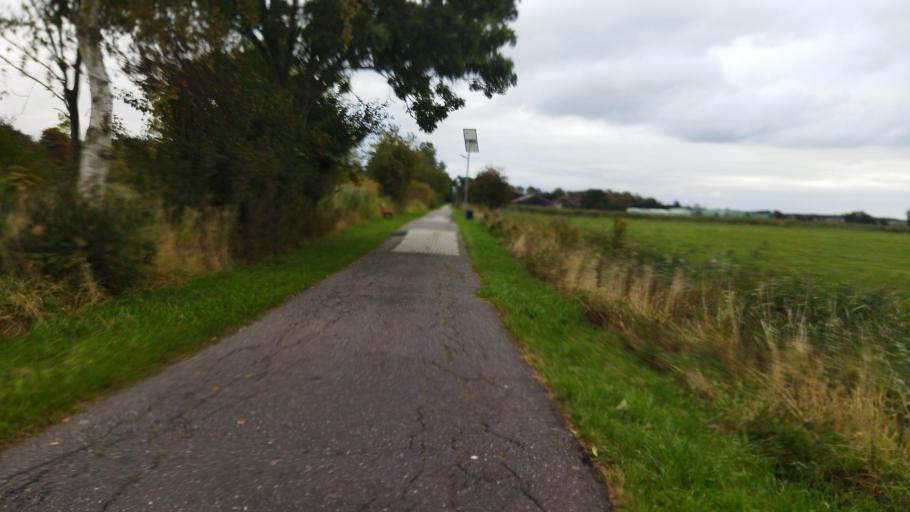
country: DE
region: Lower Saxony
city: Hinte
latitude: 53.4012
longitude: 7.1979
